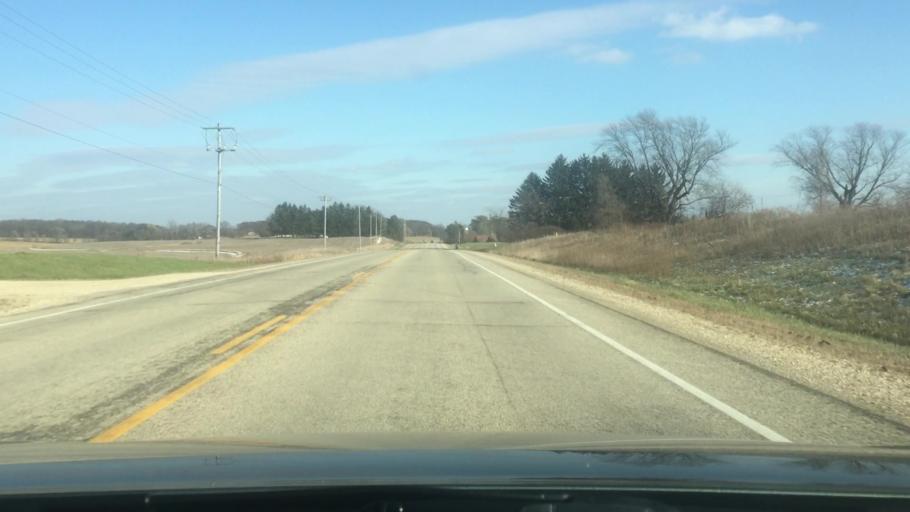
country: US
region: Wisconsin
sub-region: Jefferson County
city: Fort Atkinson
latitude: 42.9389
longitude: -88.7525
